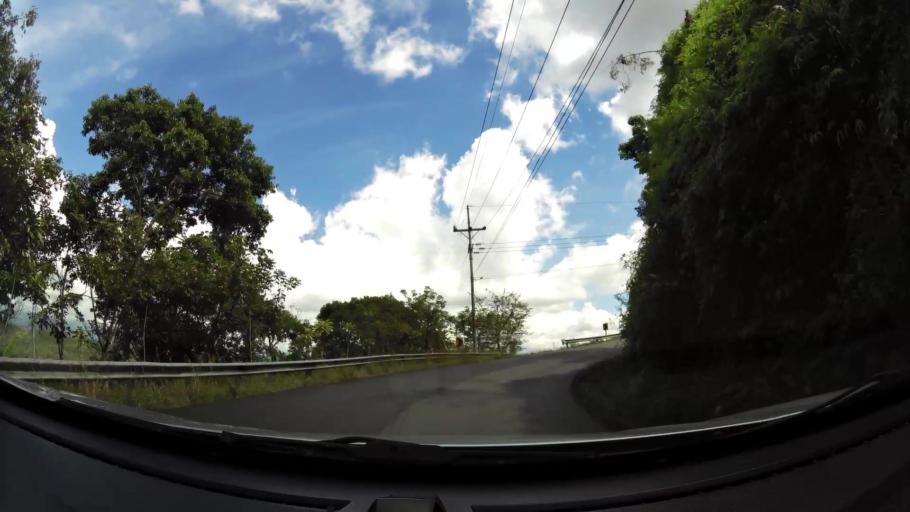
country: CR
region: San Jose
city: San Isidro
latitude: 9.3420
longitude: -83.7364
